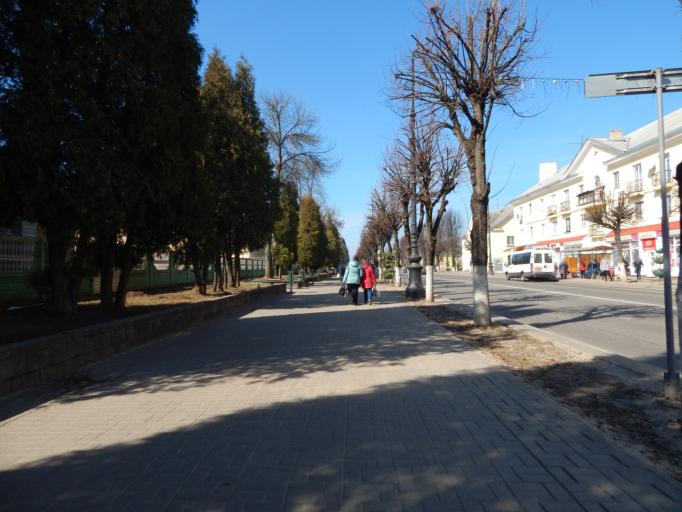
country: BY
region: Minsk
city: Horad Barysaw
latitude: 54.2222
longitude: 28.5204
